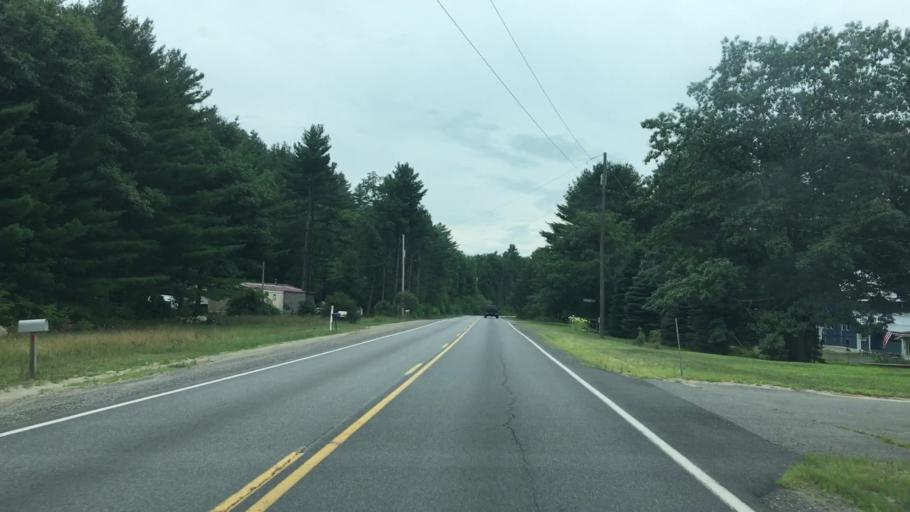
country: US
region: New York
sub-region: Clinton County
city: Peru
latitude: 44.5093
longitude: -73.5833
